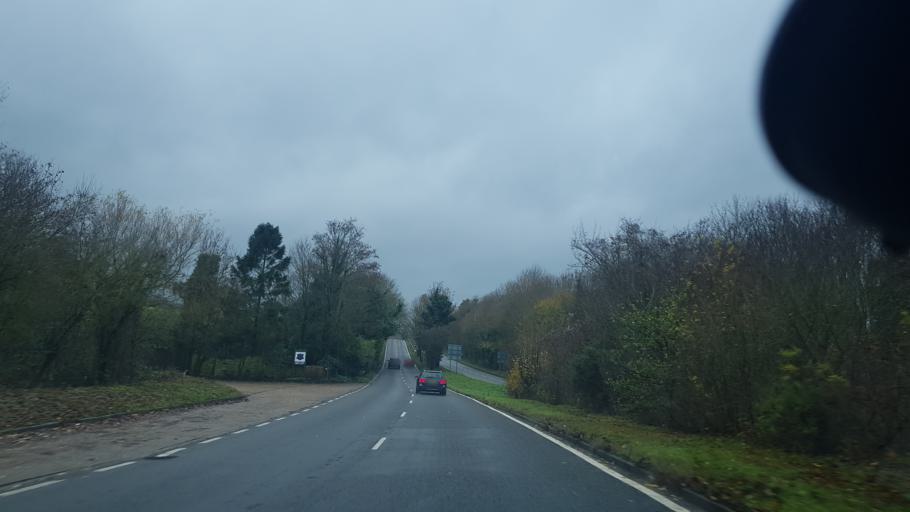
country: GB
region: England
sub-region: Surrey
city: Chilworth
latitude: 51.2482
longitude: -0.5100
